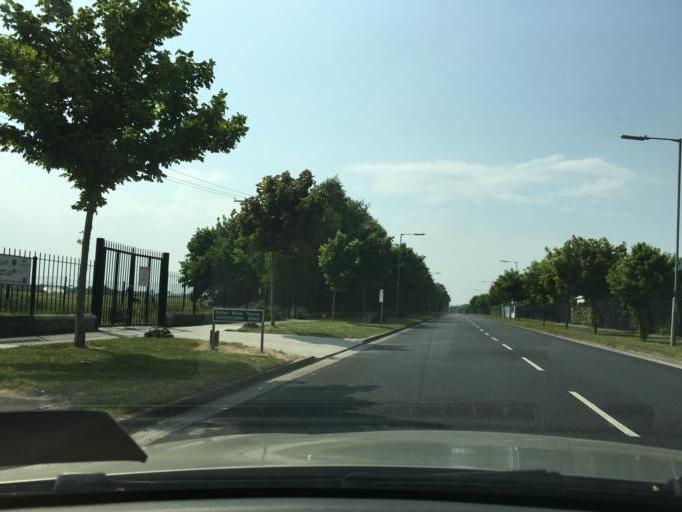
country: IE
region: Leinster
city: Hartstown
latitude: 53.4077
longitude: -6.4019
